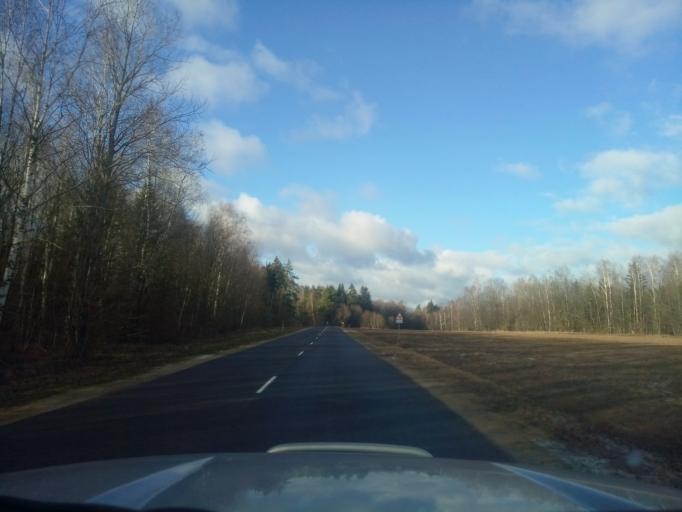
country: BY
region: Minsk
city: Kapyl'
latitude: 53.1736
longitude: 27.0203
